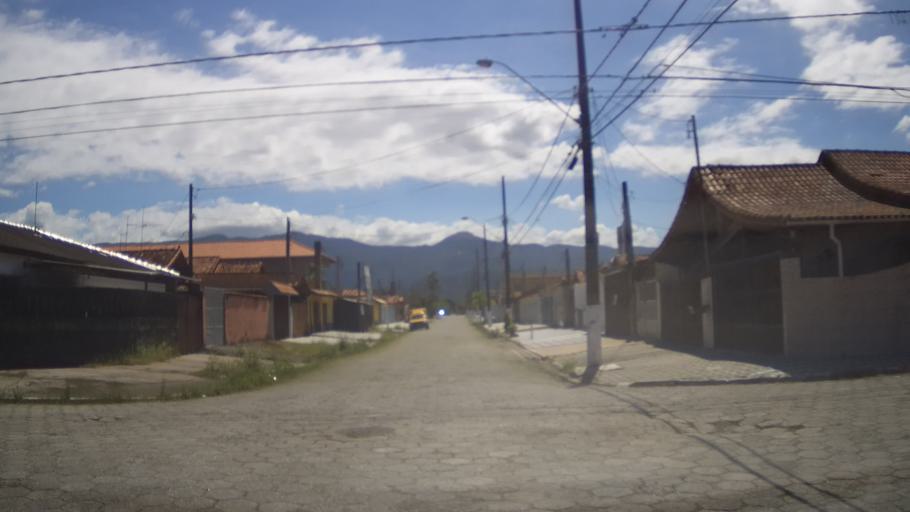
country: BR
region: Sao Paulo
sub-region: Praia Grande
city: Praia Grande
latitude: -24.0378
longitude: -46.5043
